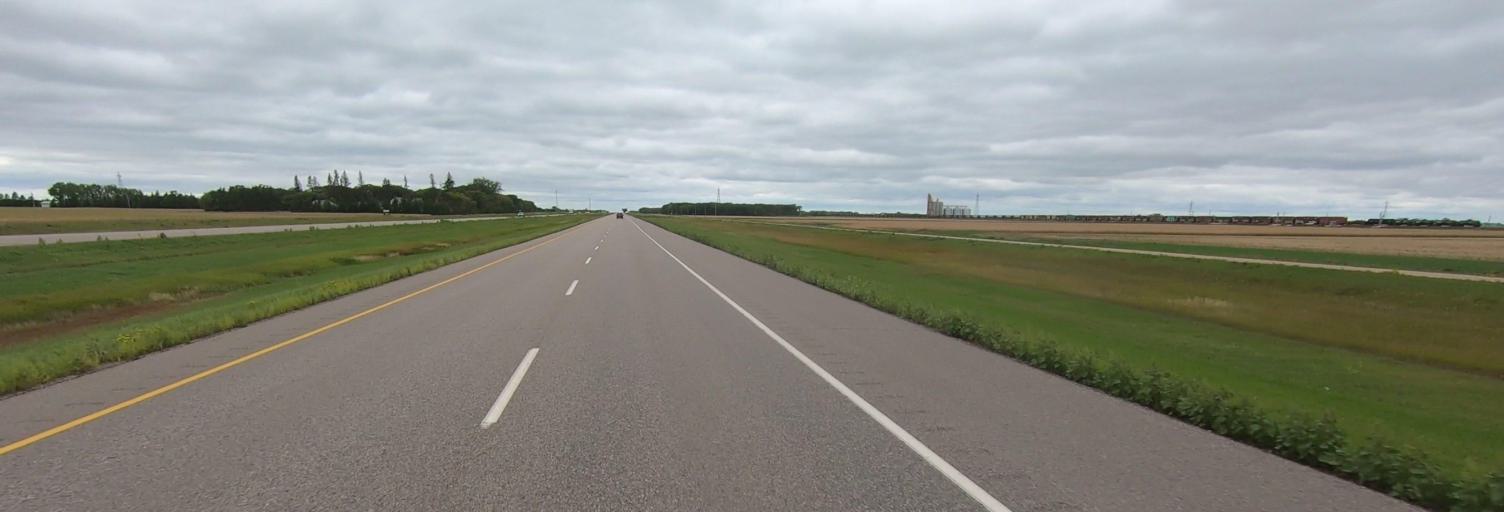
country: CA
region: Manitoba
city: Portage la Prairie
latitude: 49.9752
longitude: -98.5290
